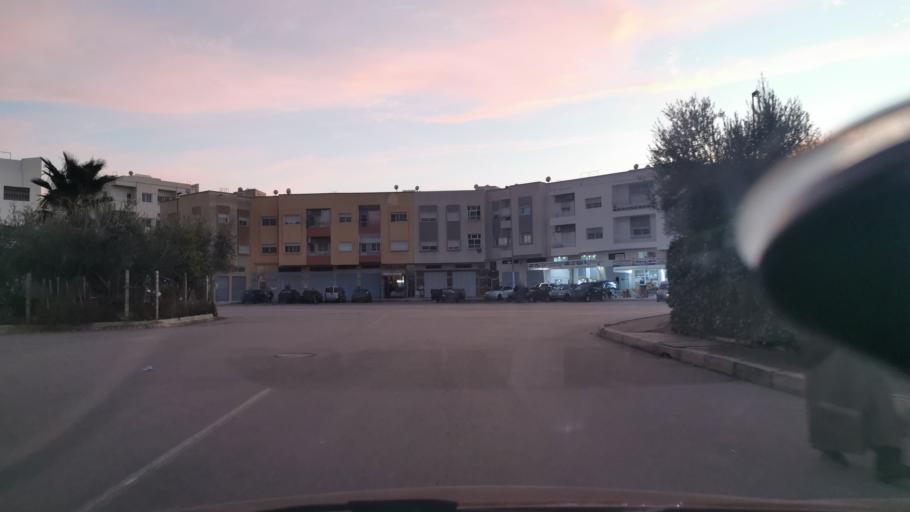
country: MA
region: Fes-Boulemane
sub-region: Fes
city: Fes
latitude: 34.0093
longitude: -4.9678
